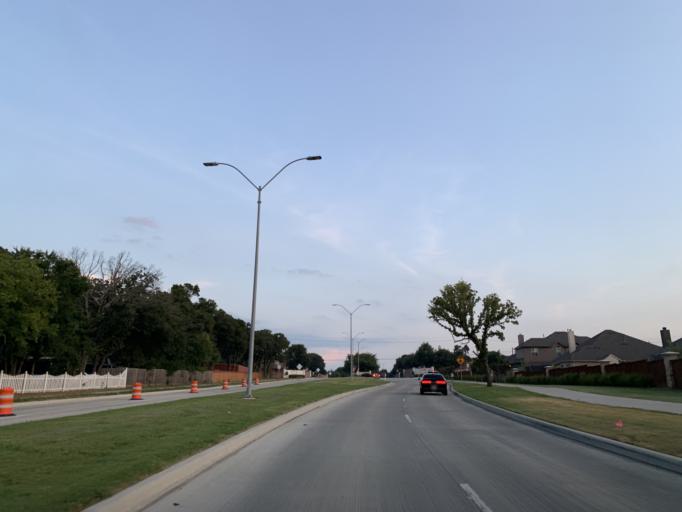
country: US
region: Texas
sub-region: Tarrant County
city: Keller
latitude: 32.9545
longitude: -97.2648
